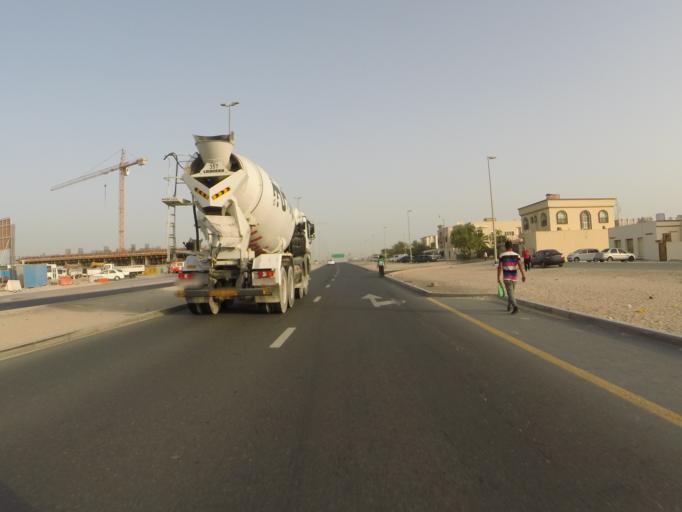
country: AE
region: Dubai
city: Dubai
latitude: 25.1608
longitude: 55.2512
